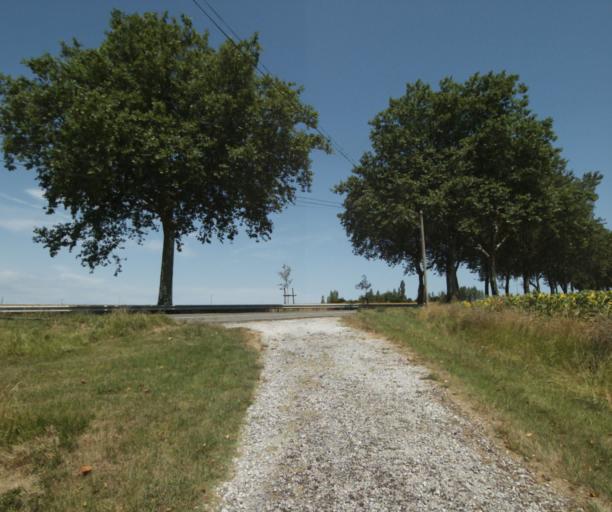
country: FR
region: Midi-Pyrenees
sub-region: Departement de la Haute-Garonne
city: Auriac-sur-Vendinelle
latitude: 43.4617
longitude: 1.8270
